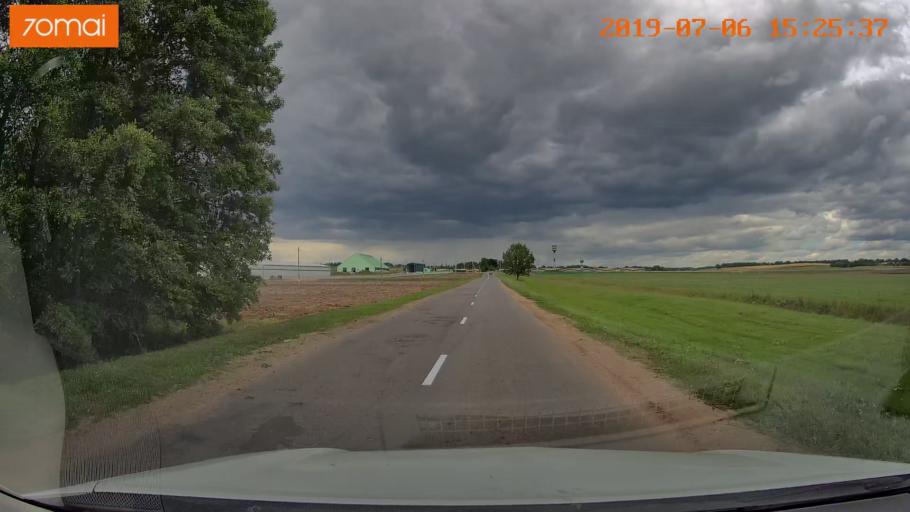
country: BY
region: Minsk
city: Valozhyn
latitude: 54.0340
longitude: 26.6046
